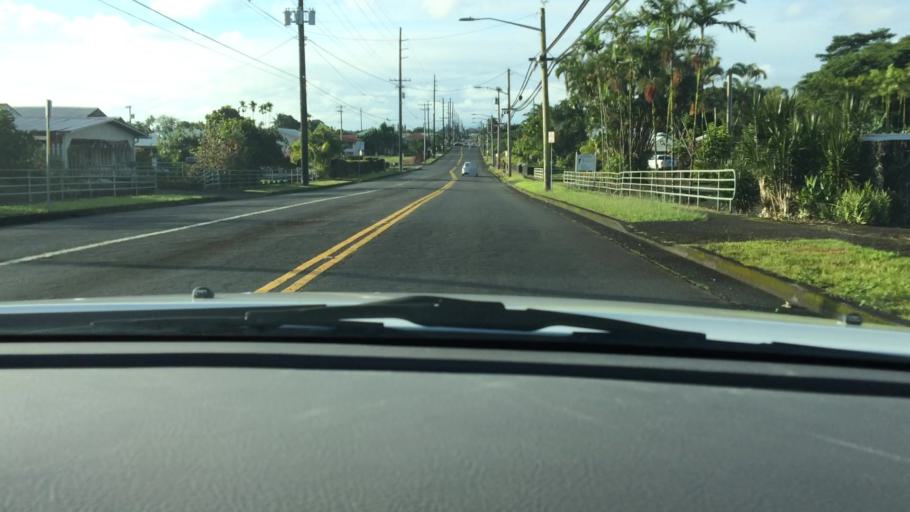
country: US
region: Hawaii
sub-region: Hawaii County
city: Hilo
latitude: 19.7091
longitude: -155.0788
